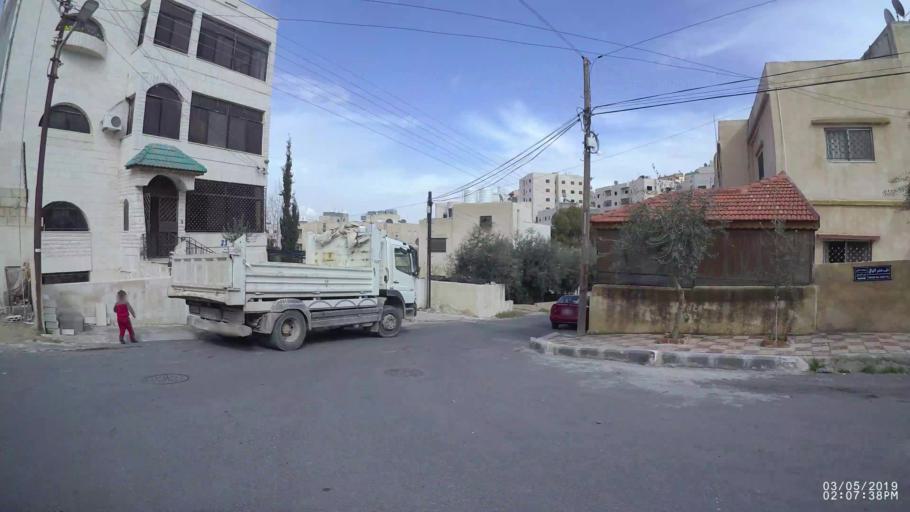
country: JO
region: Amman
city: Amman
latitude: 32.0051
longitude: 35.9388
